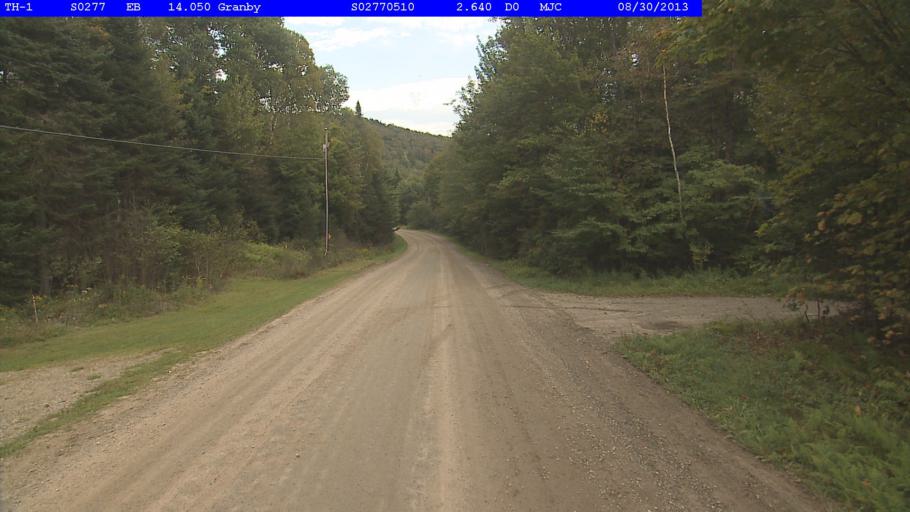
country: US
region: Vermont
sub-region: Essex County
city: Guildhall
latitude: 44.5763
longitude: -71.7148
